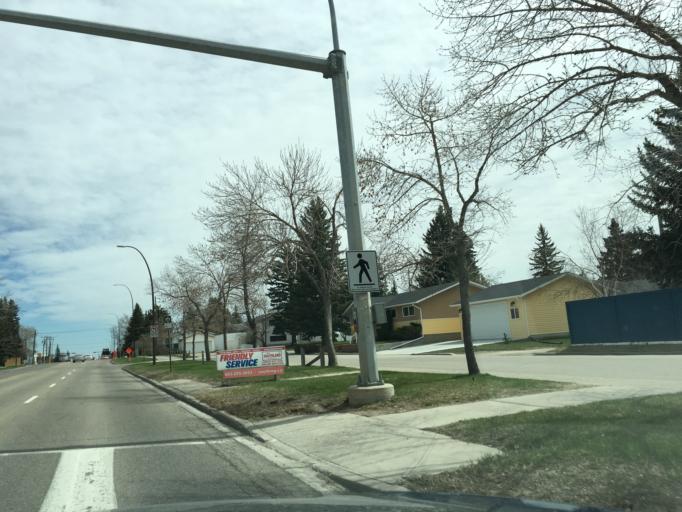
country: CA
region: Alberta
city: Calgary
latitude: 50.9796
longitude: -114.0882
